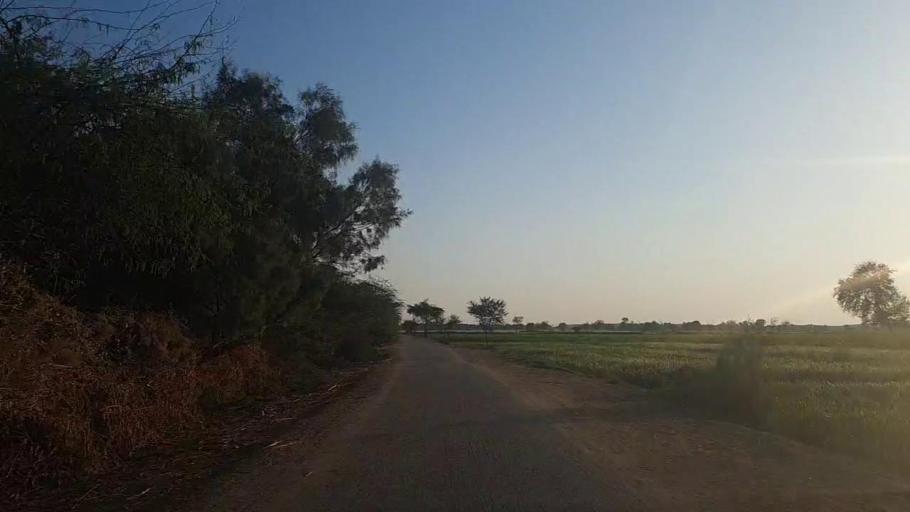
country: PK
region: Sindh
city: Jam Sahib
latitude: 26.3304
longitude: 68.6976
